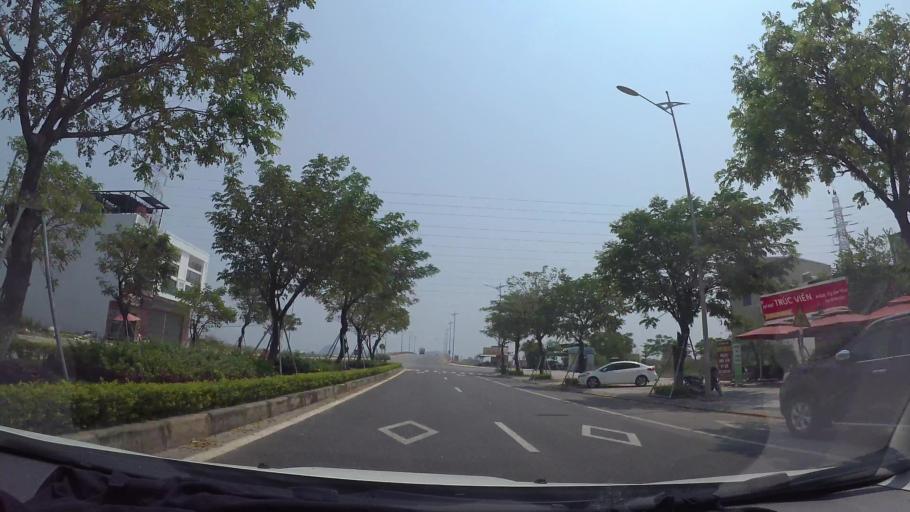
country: VN
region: Da Nang
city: Ngu Hanh Son
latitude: 16.0164
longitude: 108.2333
